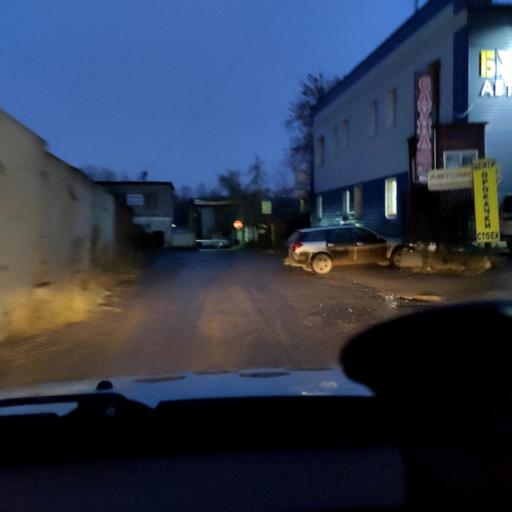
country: RU
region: Perm
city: Perm
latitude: 57.9699
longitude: 56.2052
